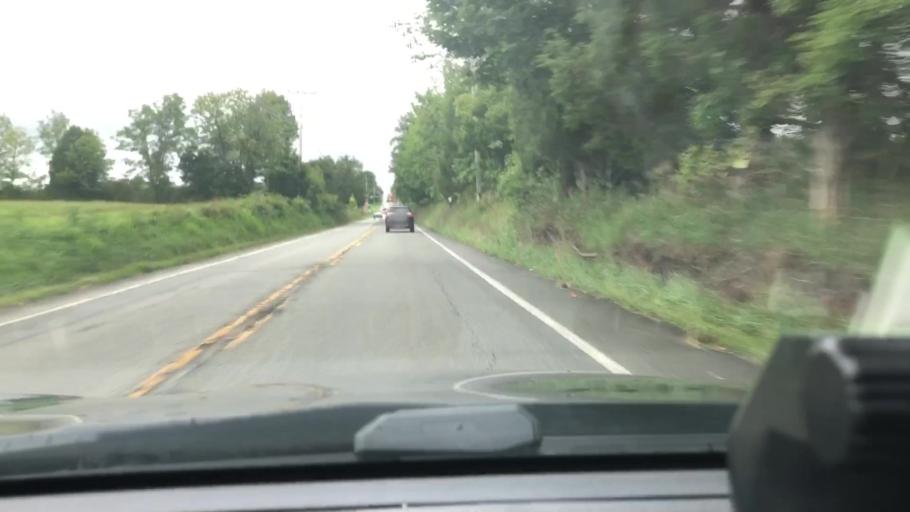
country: US
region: Pennsylvania
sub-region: Montgomery County
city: Gilbertsville
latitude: 40.3256
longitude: -75.5601
